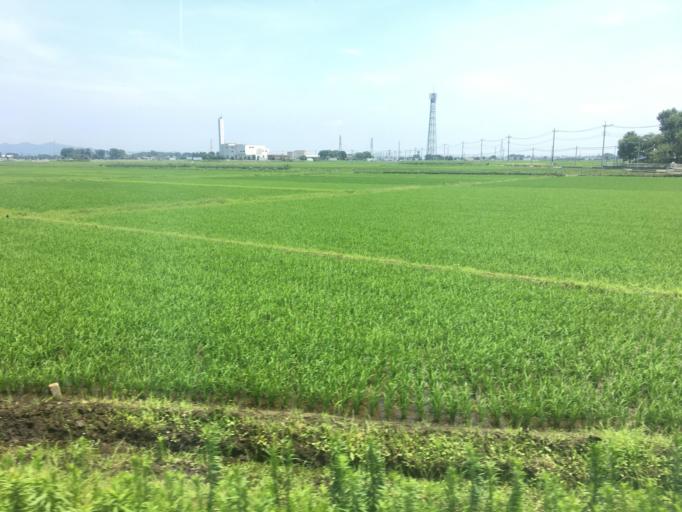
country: JP
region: Saitama
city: Menuma
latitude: 36.2627
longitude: 139.4227
